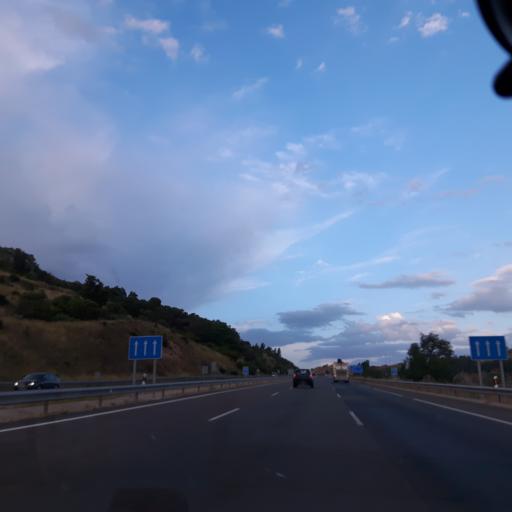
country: ES
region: Castille and Leon
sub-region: Provincia de Salamanca
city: Fresnedoso
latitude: 40.4294
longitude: -5.6977
